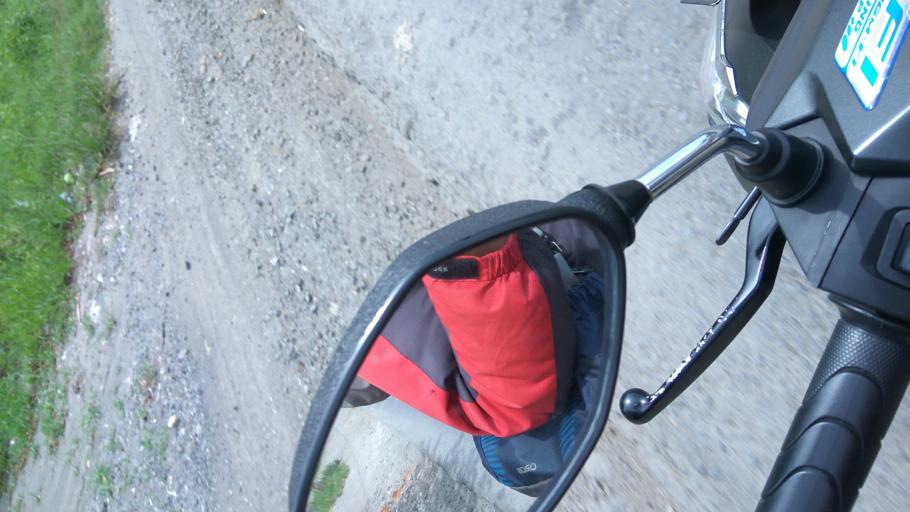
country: ID
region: Central Java
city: Mranggen
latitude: -7.0480
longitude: 110.5916
